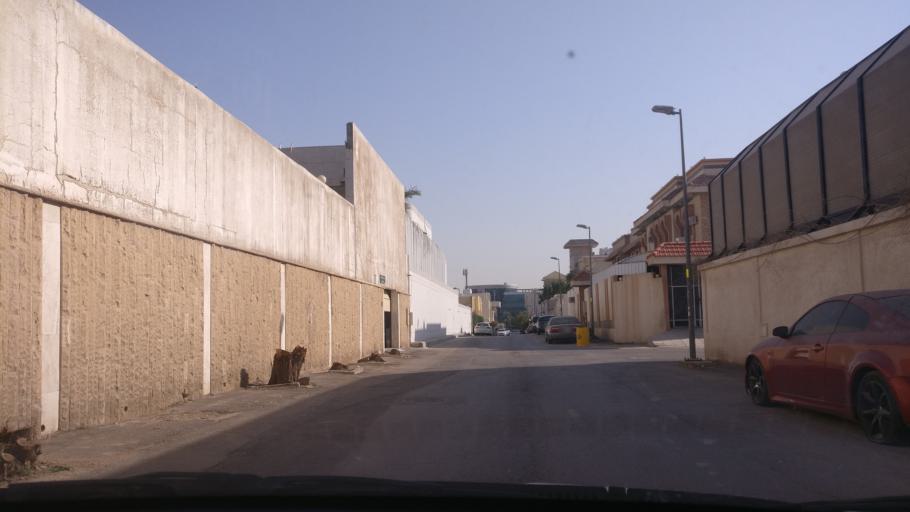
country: SA
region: Ar Riyad
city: Riyadh
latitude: 24.7003
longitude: 46.6849
